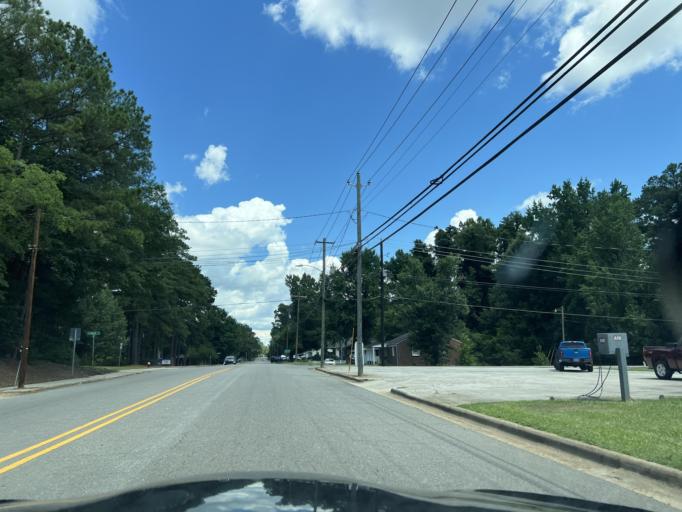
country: US
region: North Carolina
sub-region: Lee County
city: Sanford
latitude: 35.4672
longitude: -79.1670
